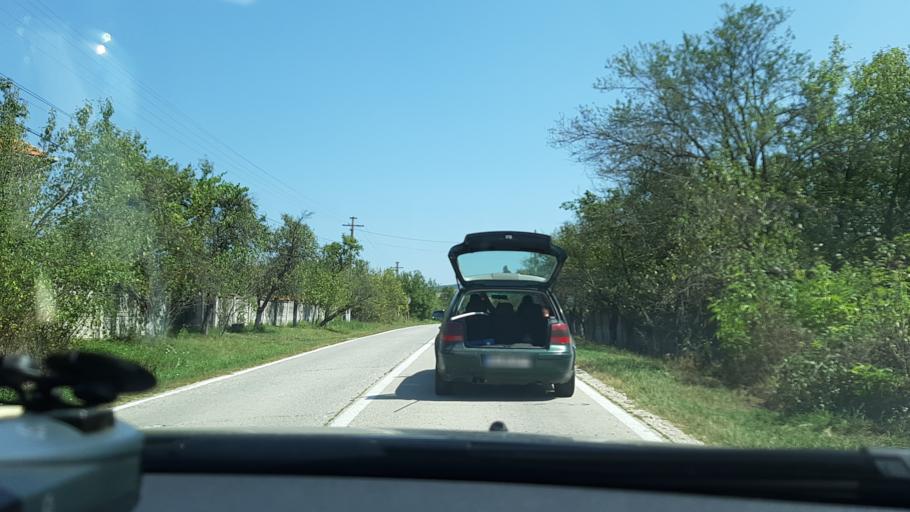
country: RO
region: Gorj
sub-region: Comuna Logresti-Mosteni
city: Logresti Mosteni
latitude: 44.8926
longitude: 23.7235
